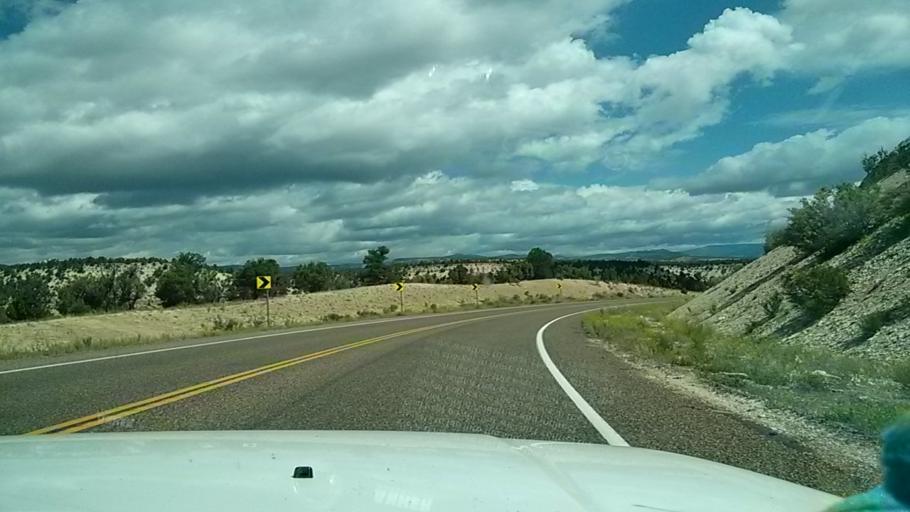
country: US
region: Utah
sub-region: Kane County
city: Kanab
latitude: 37.2037
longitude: -112.6841
